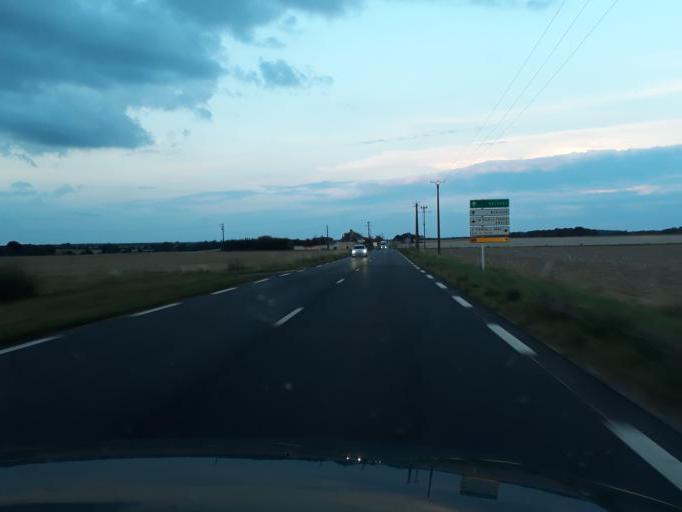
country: FR
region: Centre
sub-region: Departement du Loir-et-Cher
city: La Ville-aux-Clercs
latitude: 47.8922
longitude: 1.0792
